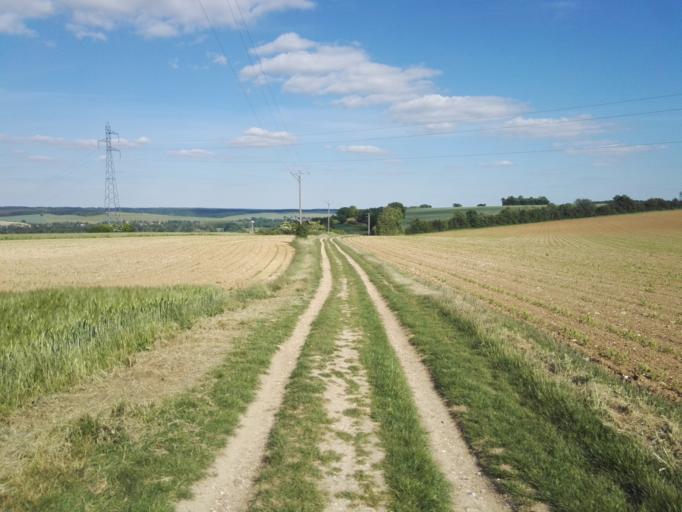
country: FR
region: Haute-Normandie
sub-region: Departement de l'Eure
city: Pacy-sur-Eure
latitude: 48.9886
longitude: 1.3753
